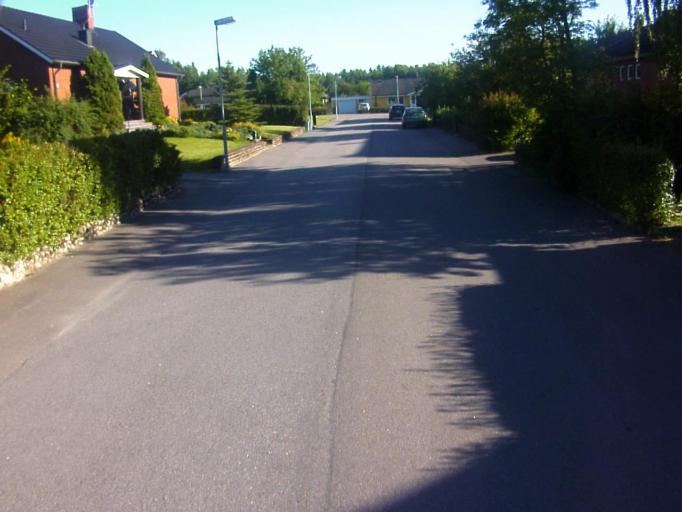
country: SE
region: Soedermanland
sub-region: Eskilstuna Kommun
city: Skogstorp
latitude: 59.3325
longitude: 16.4342
